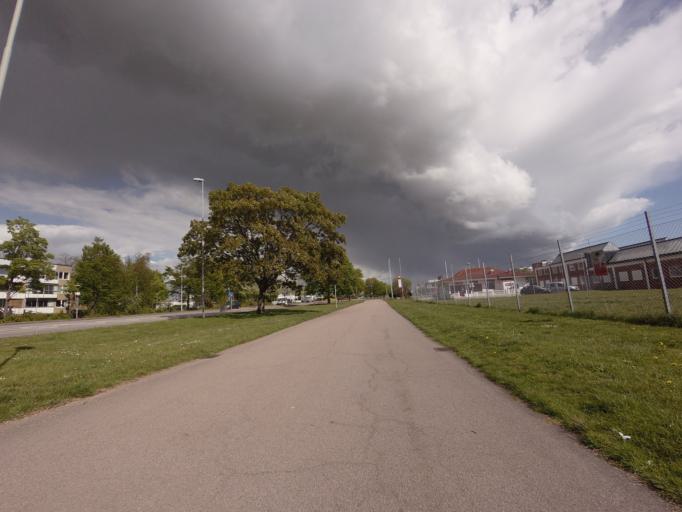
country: SE
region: Skane
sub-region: Landskrona
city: Landskrona
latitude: 55.8846
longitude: 12.8429
